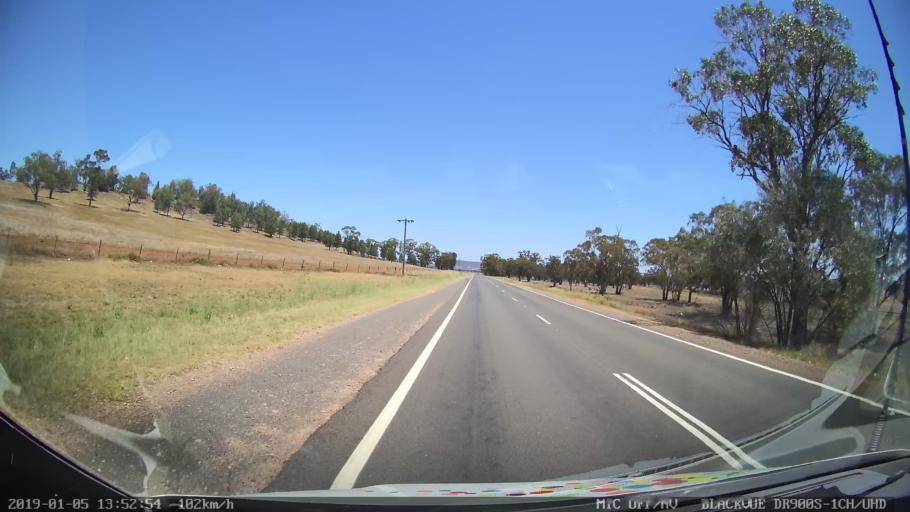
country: AU
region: New South Wales
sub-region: Gunnedah
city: Gunnedah
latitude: -31.0671
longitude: 150.2768
